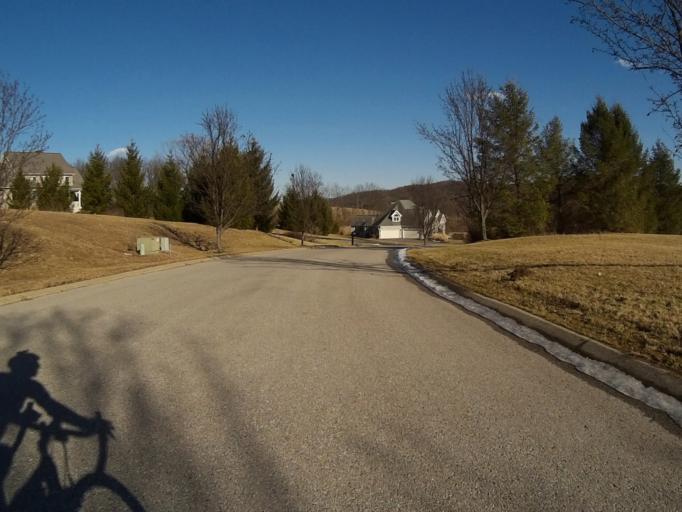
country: US
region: Pennsylvania
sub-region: Centre County
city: Park Forest Village
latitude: 40.8454
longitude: -77.9208
